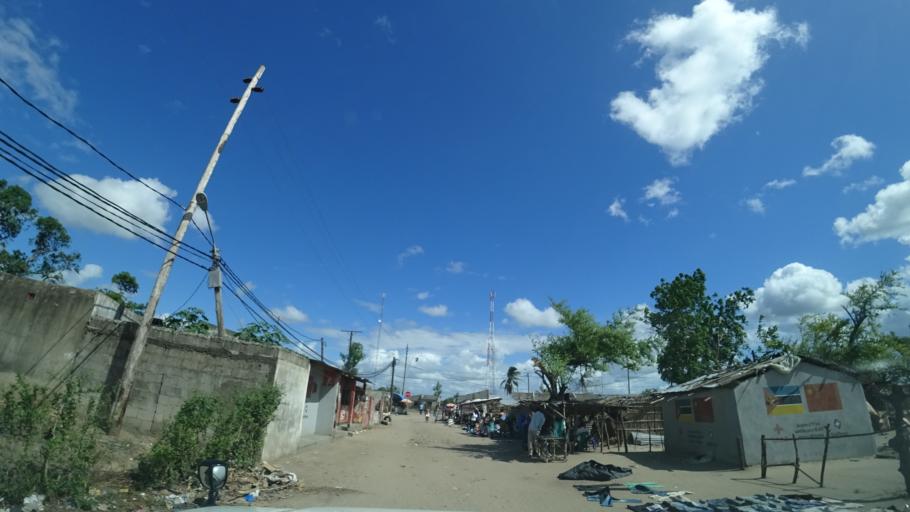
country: MZ
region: Sofala
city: Dondo
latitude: -19.4996
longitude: 34.5972
